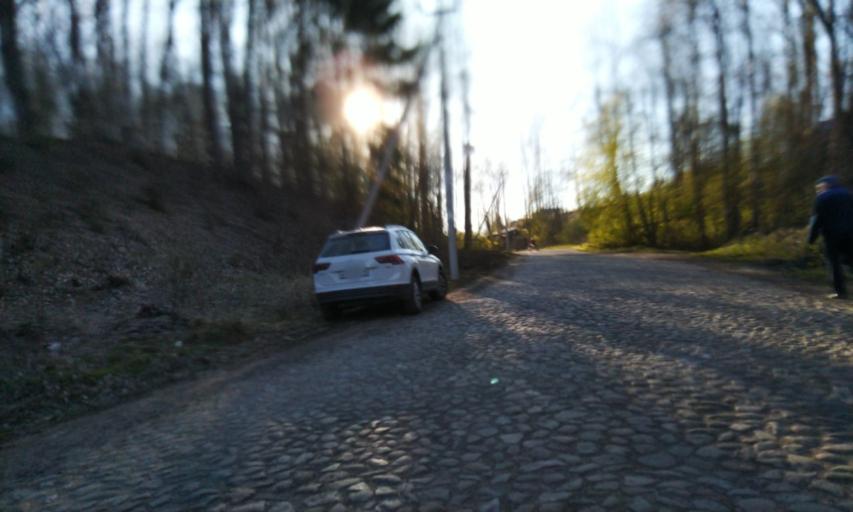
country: RU
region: Leningrad
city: Toksovo
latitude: 60.1395
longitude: 30.5670
